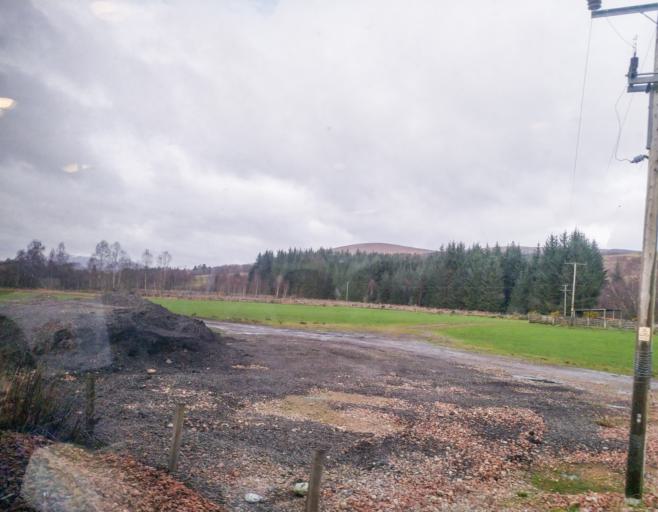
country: GB
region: Scotland
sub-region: Highland
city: Spean Bridge
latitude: 56.8887
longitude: -4.8423
